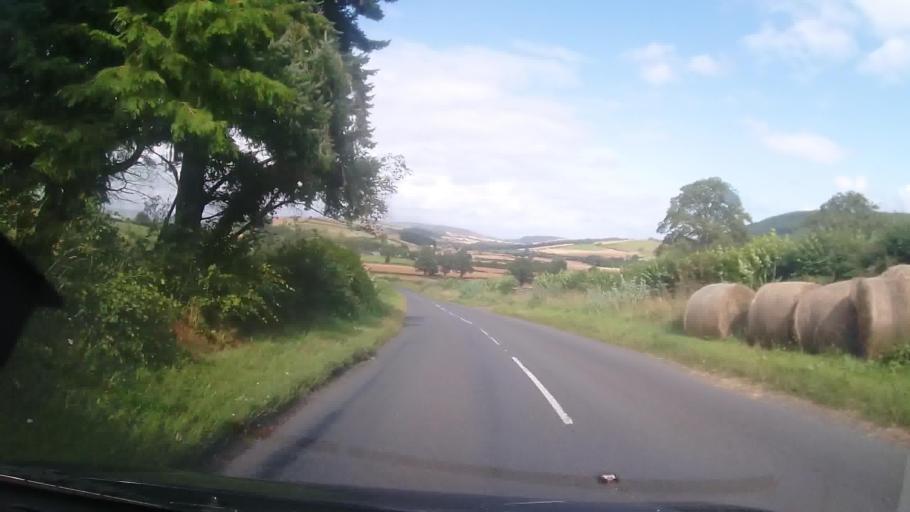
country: GB
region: England
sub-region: Shropshire
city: Acton
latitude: 52.4529
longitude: -3.0215
